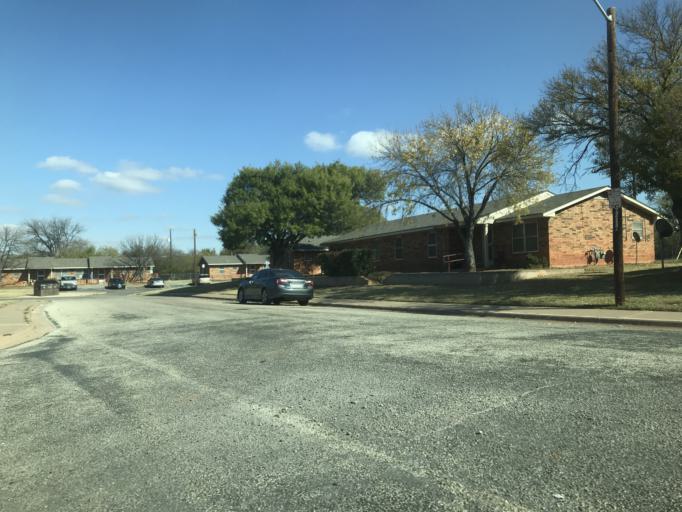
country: US
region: Texas
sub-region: Taylor County
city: Abilene
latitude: 32.4587
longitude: -99.7775
